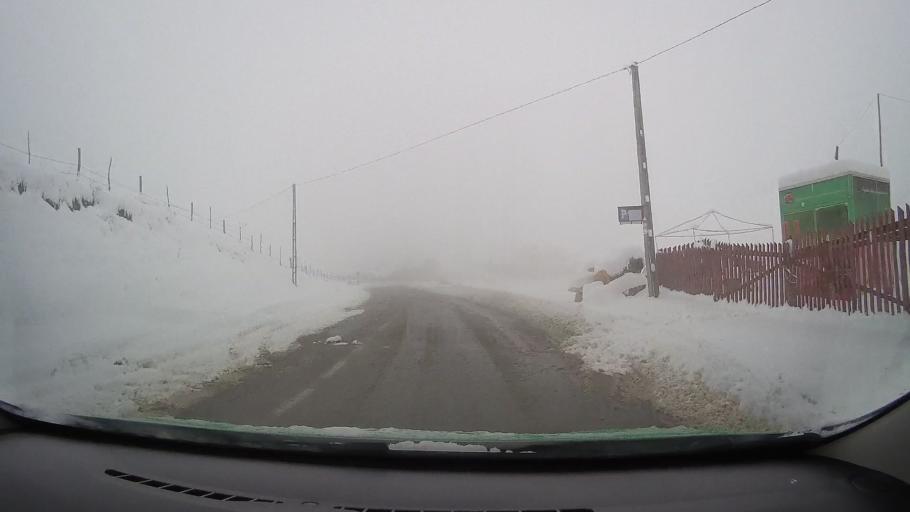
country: RO
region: Sibiu
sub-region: Comuna Jina
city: Jina
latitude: 45.7730
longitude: 23.6647
